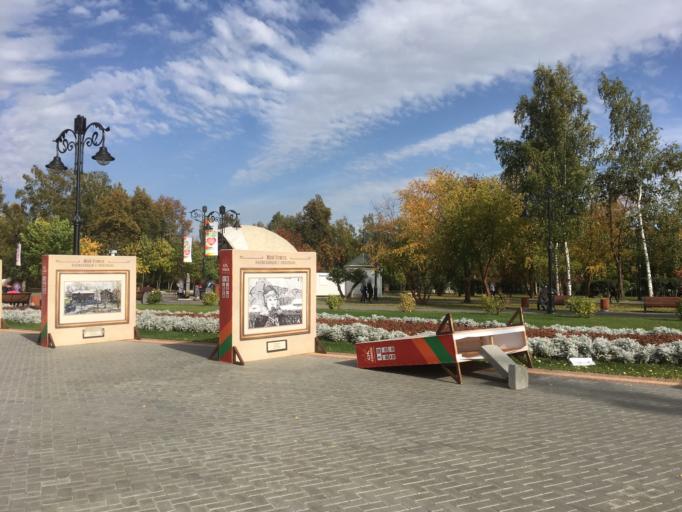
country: RU
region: Tomsk
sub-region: Tomskiy Rayon
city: Tomsk
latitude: 56.4735
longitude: 84.9512
